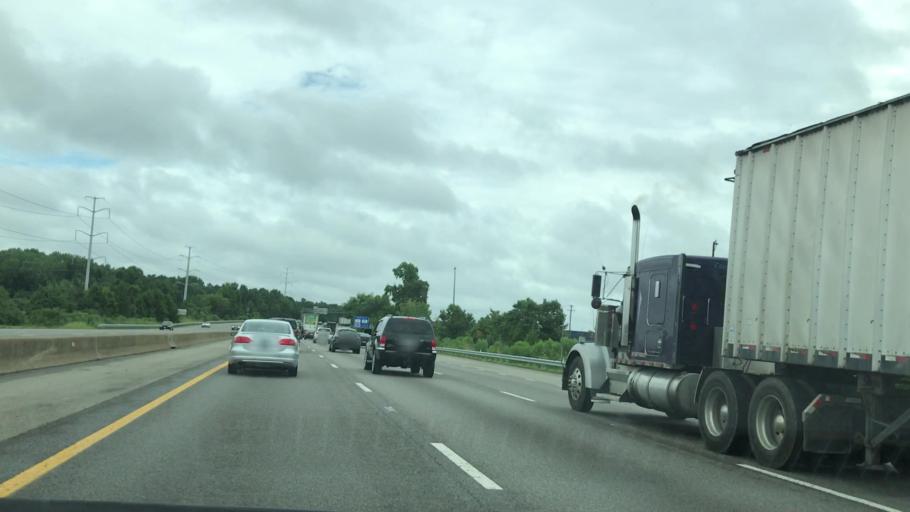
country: US
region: Virginia
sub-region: Chesterfield County
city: Bensley
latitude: 37.4528
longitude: -77.4243
